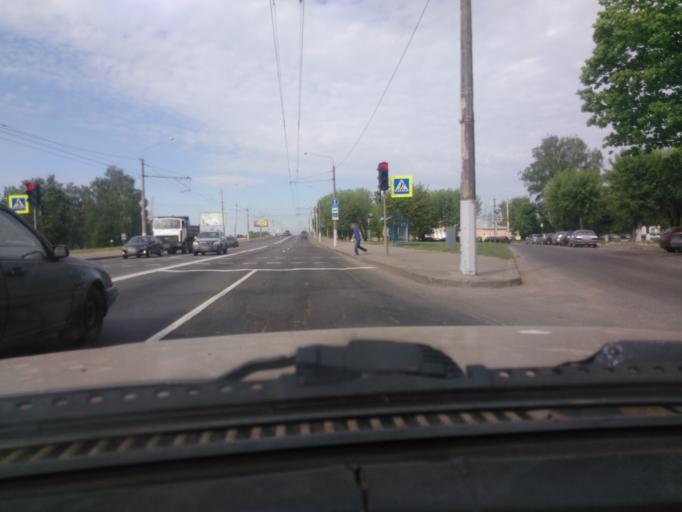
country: BY
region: Mogilev
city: Buynichy
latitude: 53.8914
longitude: 30.2962
